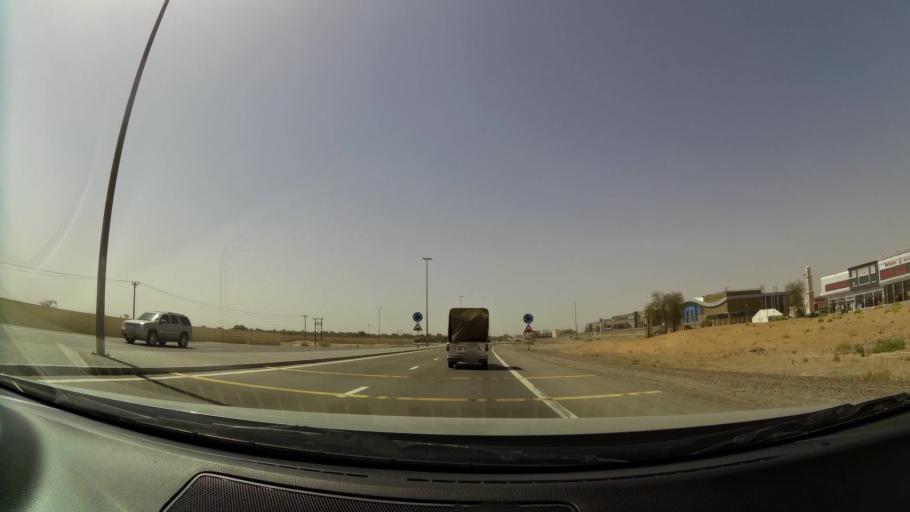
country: OM
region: Al Buraimi
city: Al Buraymi
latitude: 24.3077
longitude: 55.7611
